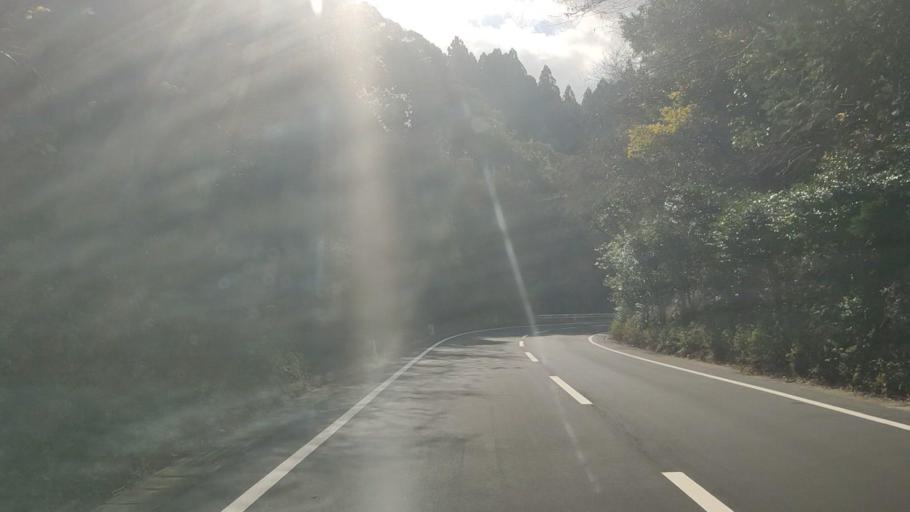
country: JP
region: Kagoshima
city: Okuchi-shinohara
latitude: 31.9590
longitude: 130.7346
